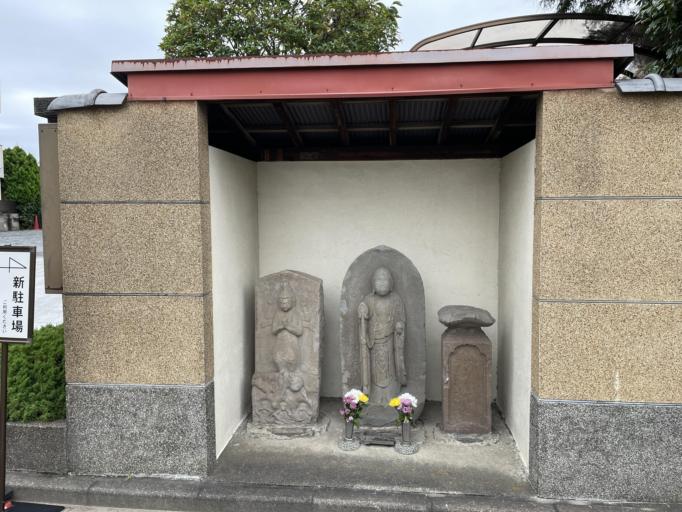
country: JP
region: Saitama
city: Soka
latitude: 35.8045
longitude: 139.7748
